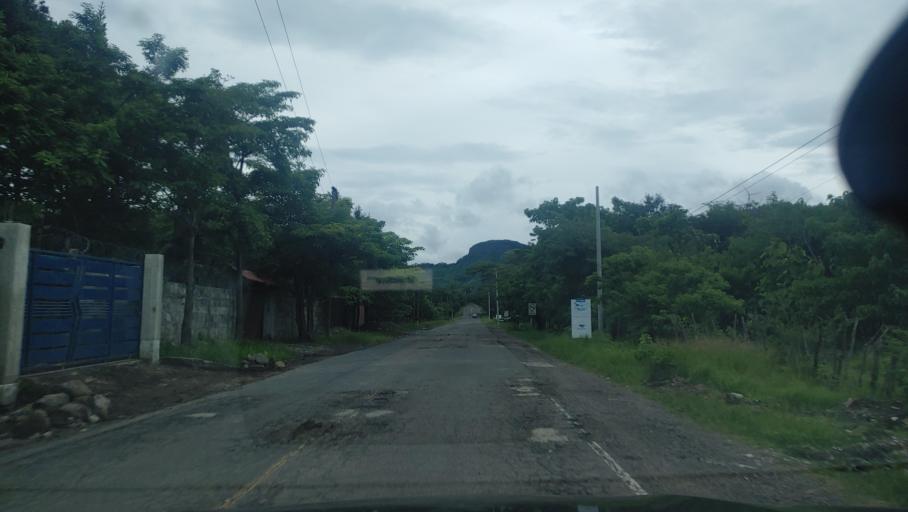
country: HN
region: Choluteca
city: Corpus
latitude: 13.3620
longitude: -86.9795
